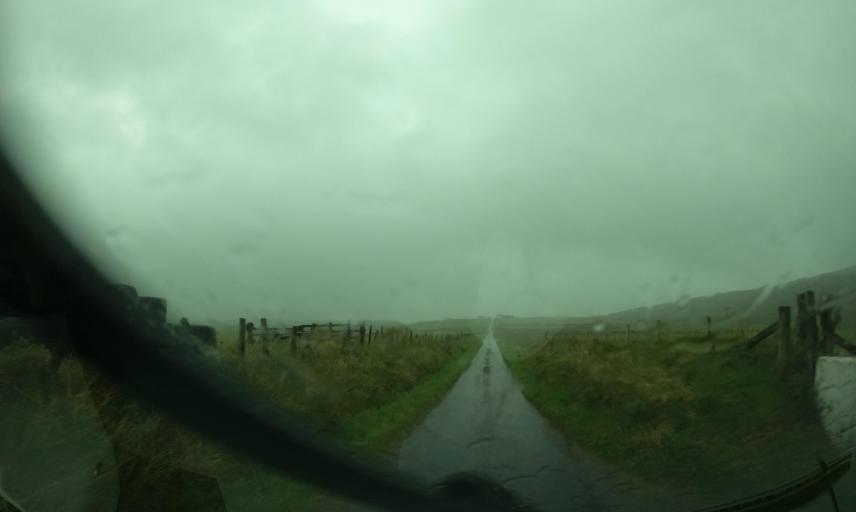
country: GB
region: Scotland
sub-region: Eilean Siar
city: Barra
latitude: 56.4580
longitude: -6.9373
